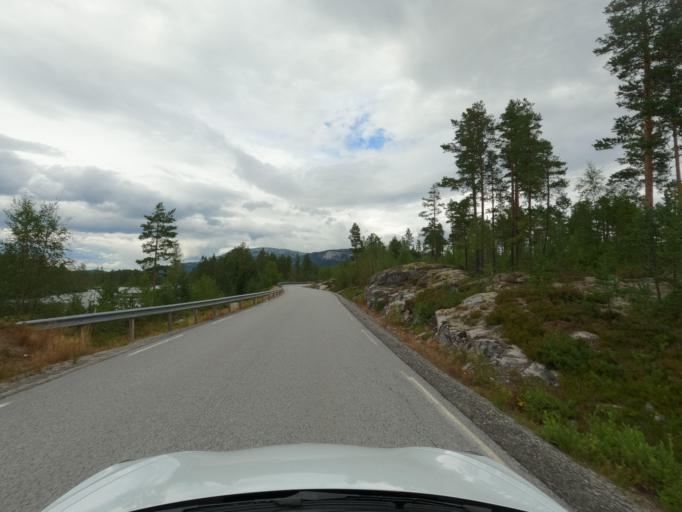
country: NO
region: Telemark
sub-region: Notodden
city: Notodden
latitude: 59.7093
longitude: 9.1511
